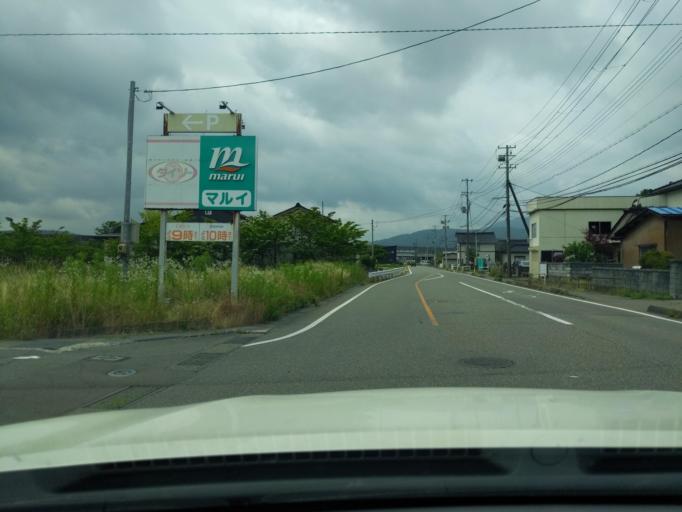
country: JP
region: Niigata
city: Kashiwazaki
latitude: 37.3461
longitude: 138.5689
